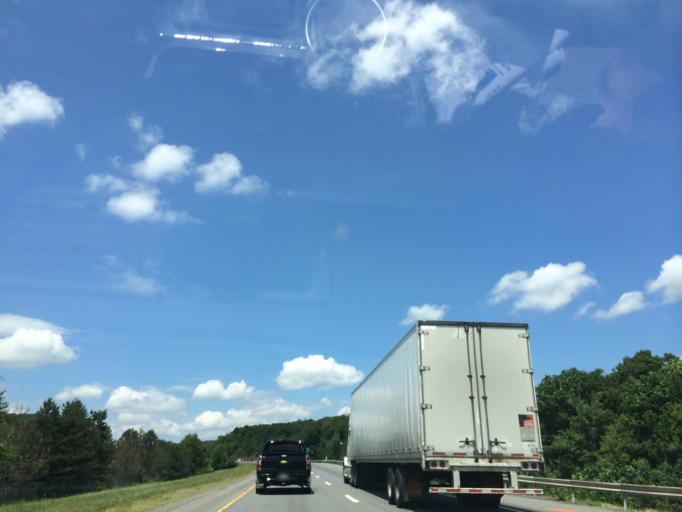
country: US
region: Pennsylvania
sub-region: Lackawanna County
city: Mount Cobb
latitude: 41.4017
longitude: -75.4902
